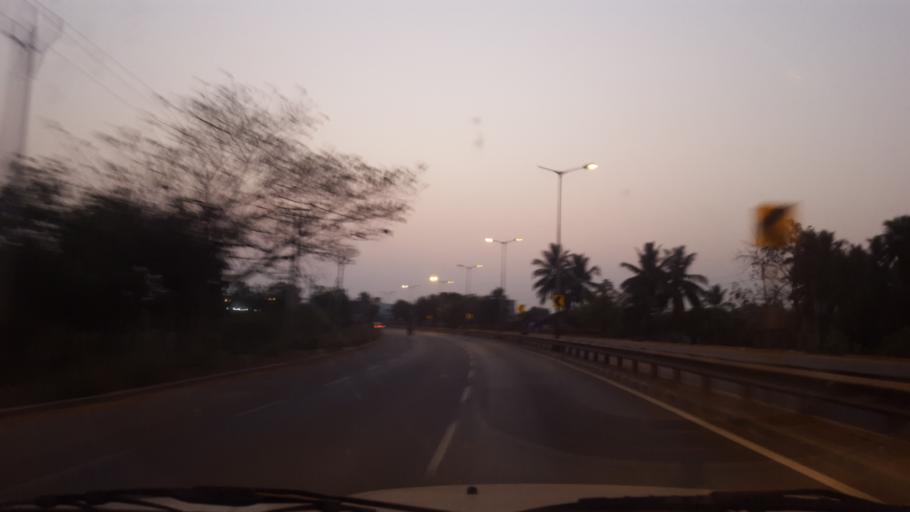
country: IN
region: Andhra Pradesh
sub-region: East Godavari
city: Peddapuram
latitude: 17.1581
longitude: 81.9938
